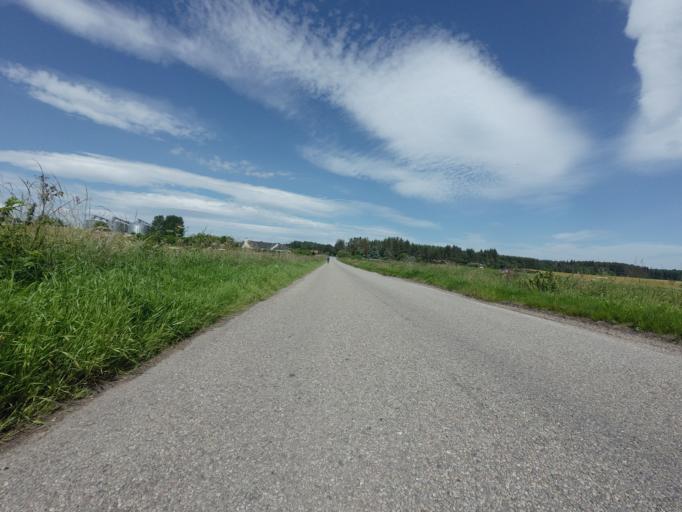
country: GB
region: Scotland
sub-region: Highland
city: Inverness
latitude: 57.5286
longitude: -4.3193
